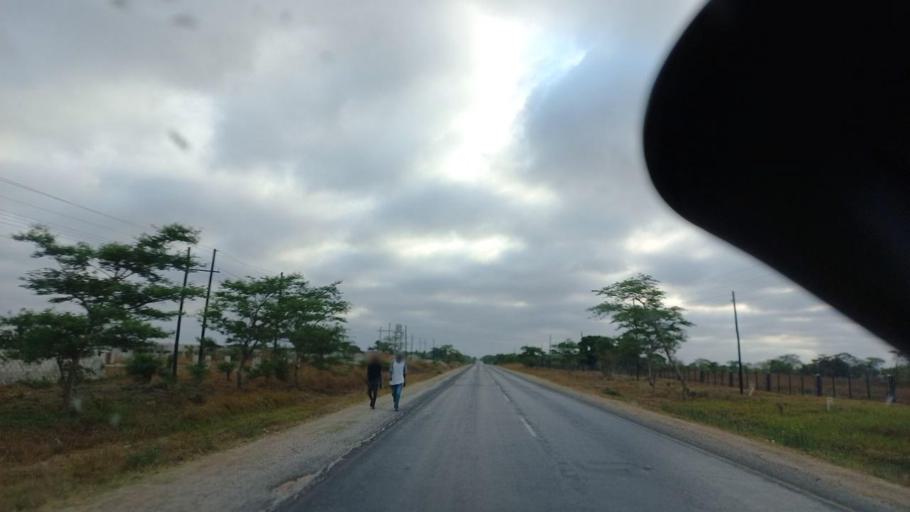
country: ZM
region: Lusaka
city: Chongwe
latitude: -15.3516
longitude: 28.4924
